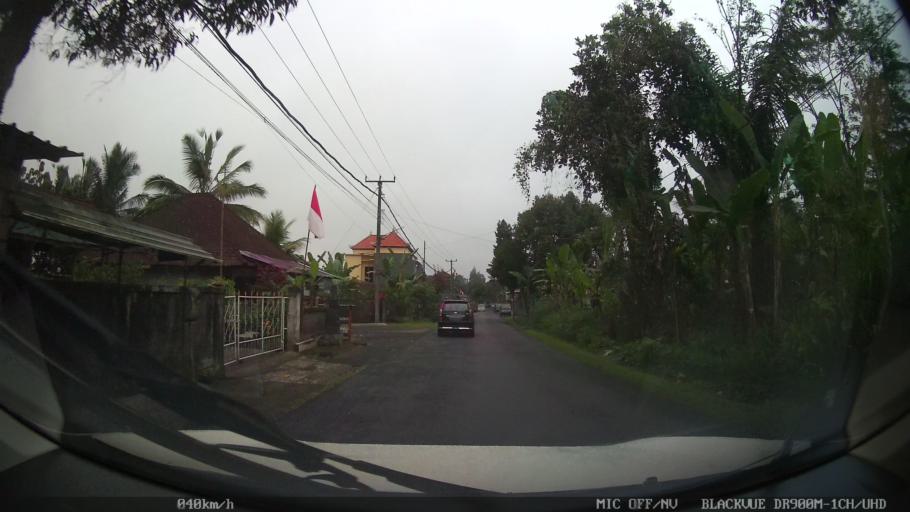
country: ID
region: Bali
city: Banjar Ponggang
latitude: -8.3786
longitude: 115.2667
